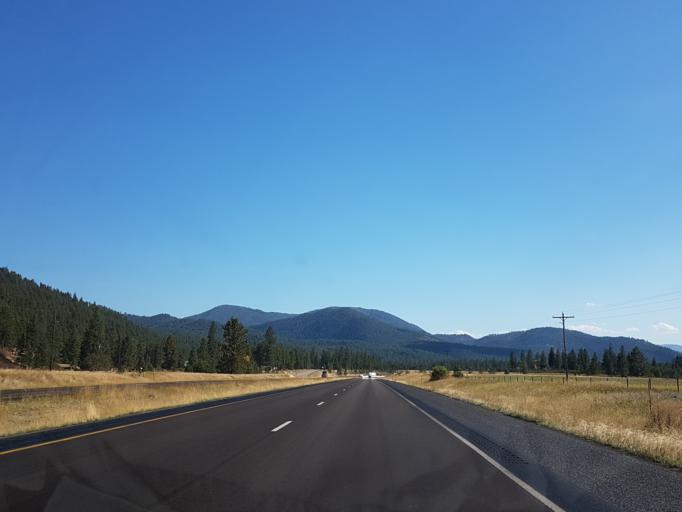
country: US
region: Montana
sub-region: Mineral County
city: Superior
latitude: 47.1381
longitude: -114.8059
